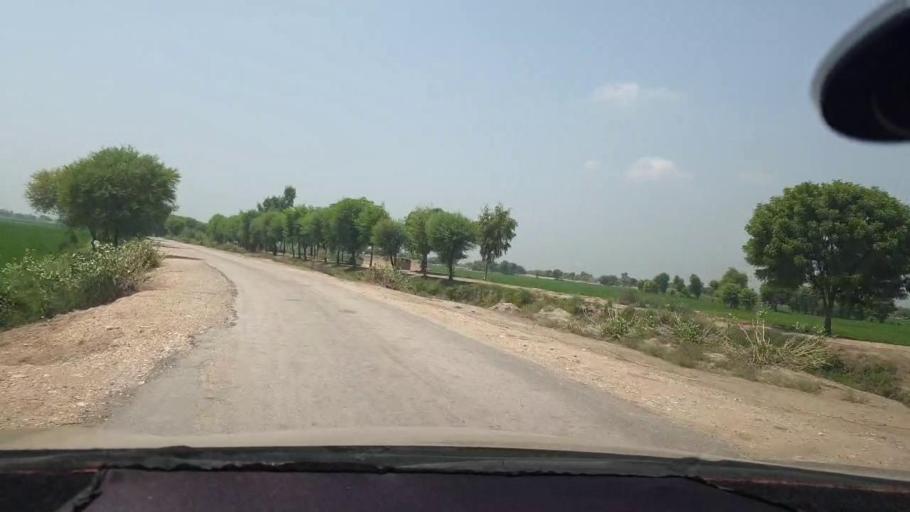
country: PK
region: Sindh
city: Kambar
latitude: 27.6641
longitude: 67.9225
